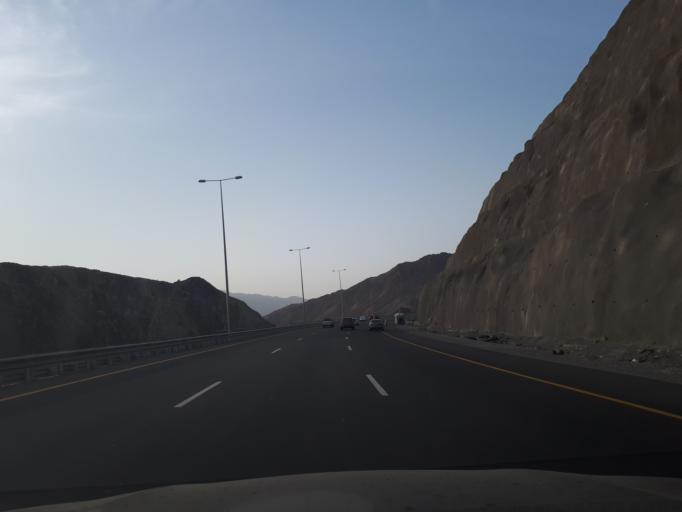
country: OM
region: Muhafazat ad Dakhiliyah
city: Bidbid
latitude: 23.3513
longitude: 58.0913
